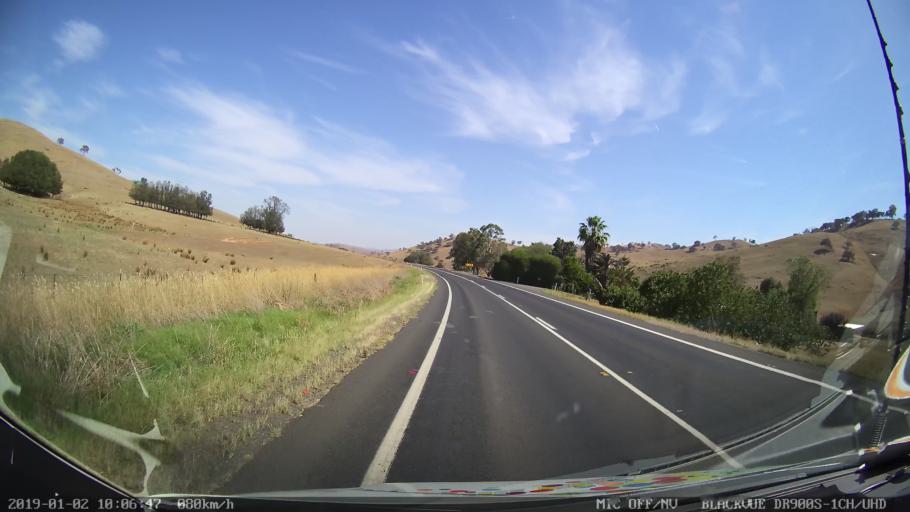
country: AU
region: New South Wales
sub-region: Gundagai
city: Gundagai
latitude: -35.1452
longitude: 148.1187
